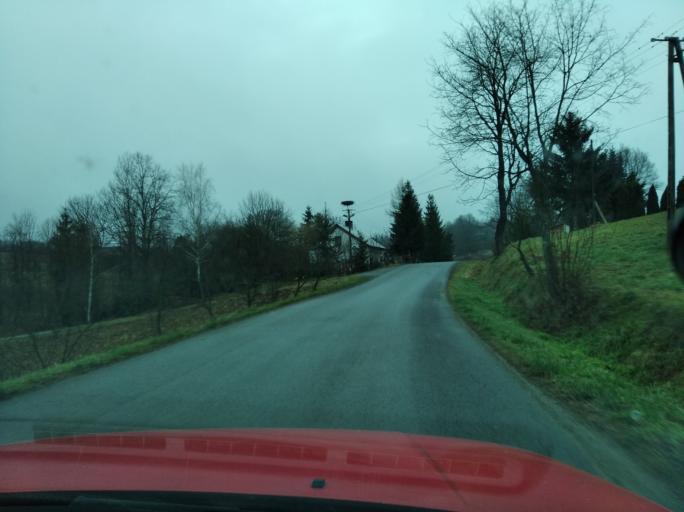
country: PL
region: Subcarpathian Voivodeship
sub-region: Powiat przemyski
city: Nienadowa
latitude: 49.8700
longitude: 22.4192
